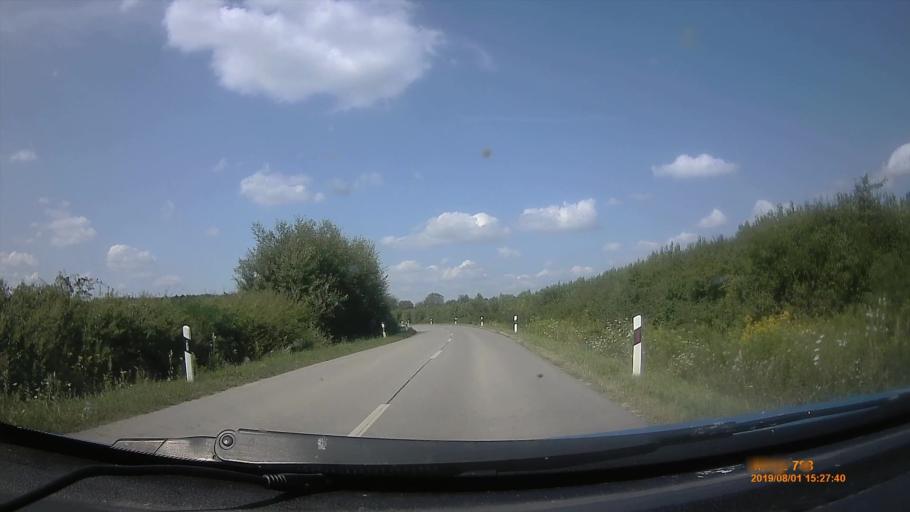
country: HU
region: Baranya
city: Sellye
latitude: 45.9084
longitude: 17.8637
